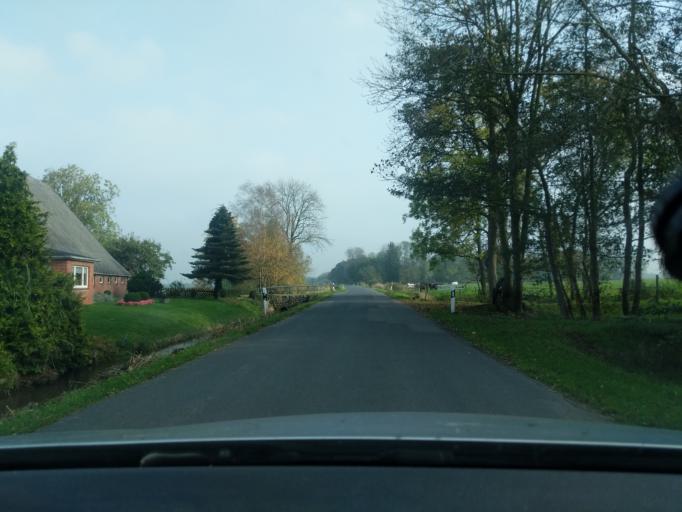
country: DE
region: Lower Saxony
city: Neuenkirchen
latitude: 53.7366
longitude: 8.8801
